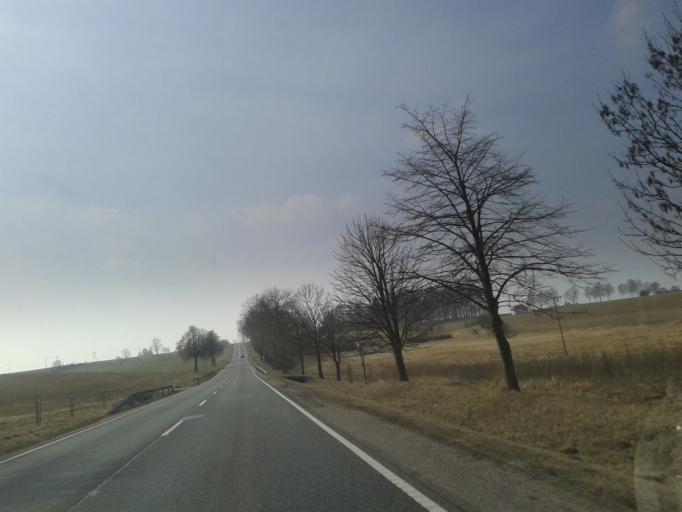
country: PL
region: Pomeranian Voivodeship
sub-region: Powiat czluchowski
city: Debrzno
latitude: 53.6113
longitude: 17.1664
